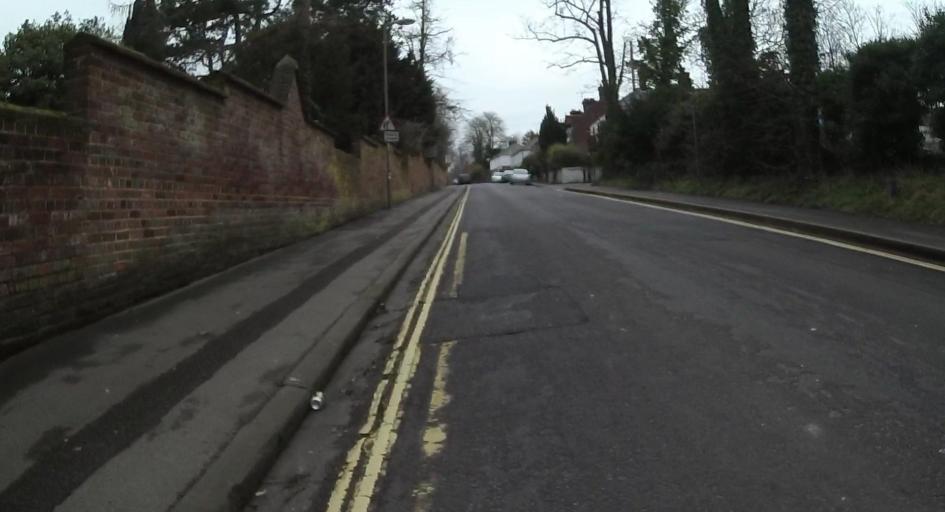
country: GB
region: England
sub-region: Hampshire
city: Basingstoke
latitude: 51.2695
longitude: -1.0888
